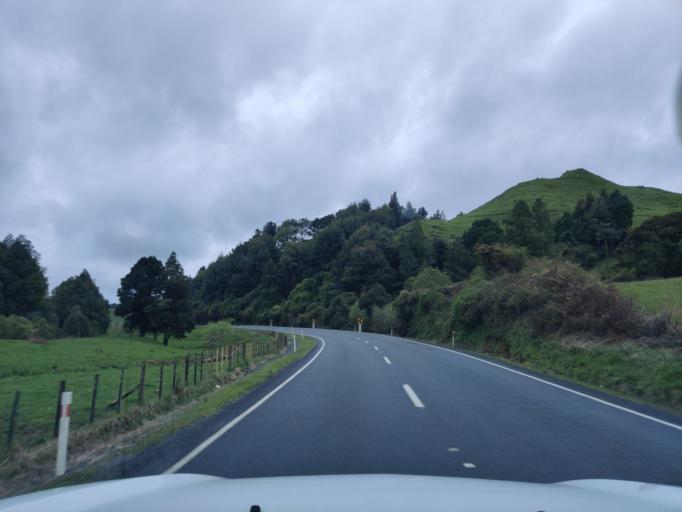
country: NZ
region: Waikato
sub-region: Otorohanga District
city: Otorohanga
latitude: -38.5430
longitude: 175.1831
